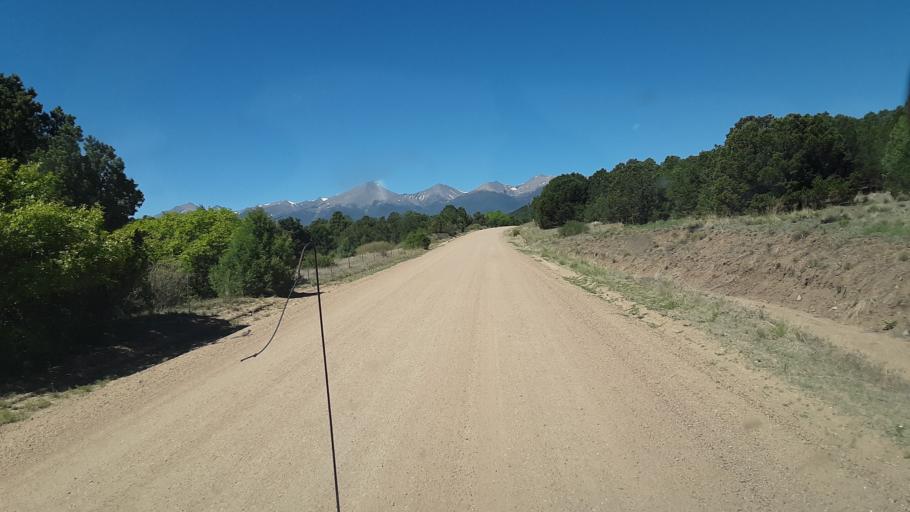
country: US
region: Colorado
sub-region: Custer County
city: Westcliffe
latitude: 38.2736
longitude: -105.5376
